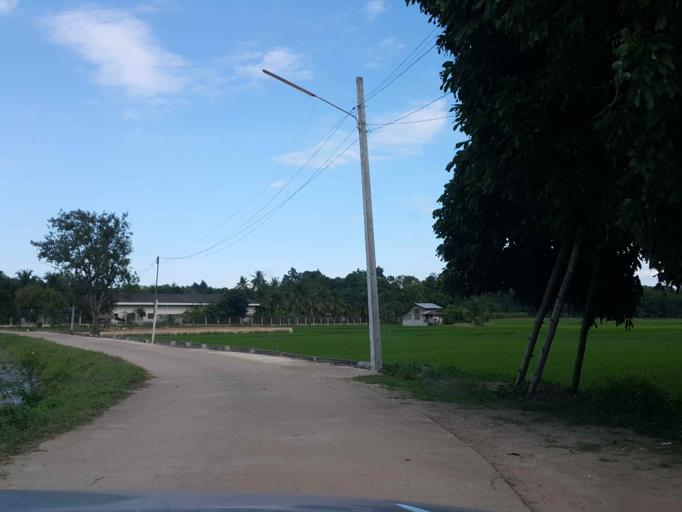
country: TH
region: Chiang Mai
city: Mae Taeng
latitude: 18.9718
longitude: 98.9164
